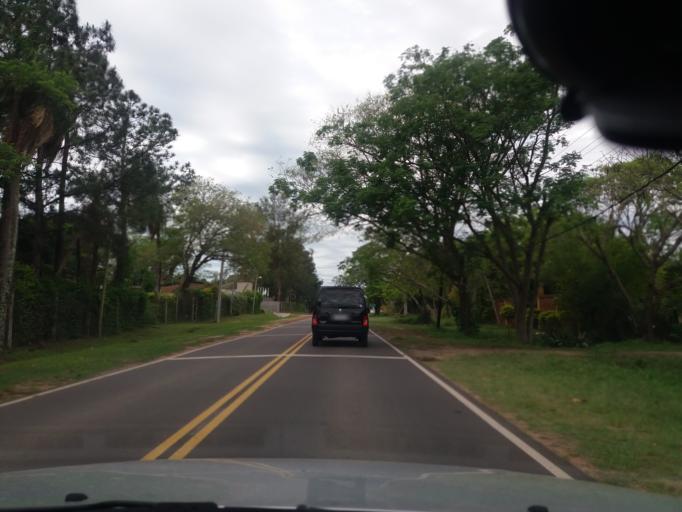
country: AR
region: Corrientes
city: Corrientes
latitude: -27.4510
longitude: -58.7351
